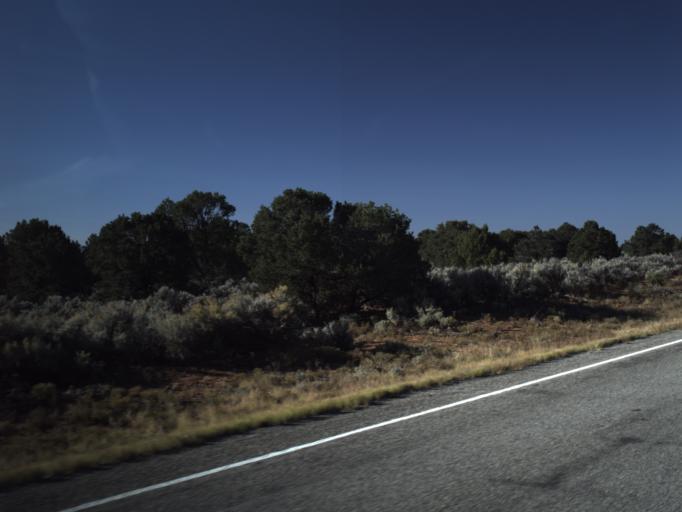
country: US
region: Utah
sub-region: San Juan County
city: Blanding
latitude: 37.5838
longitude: -109.9079
